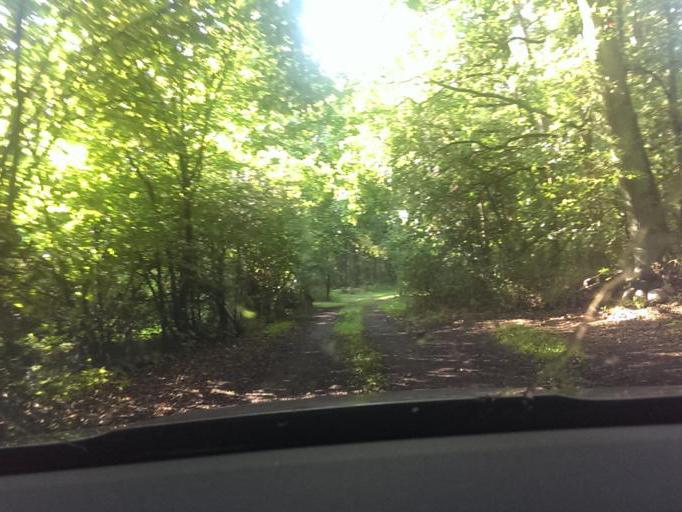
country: DE
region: Lower Saxony
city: Elze
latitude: 52.5725
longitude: 9.7981
